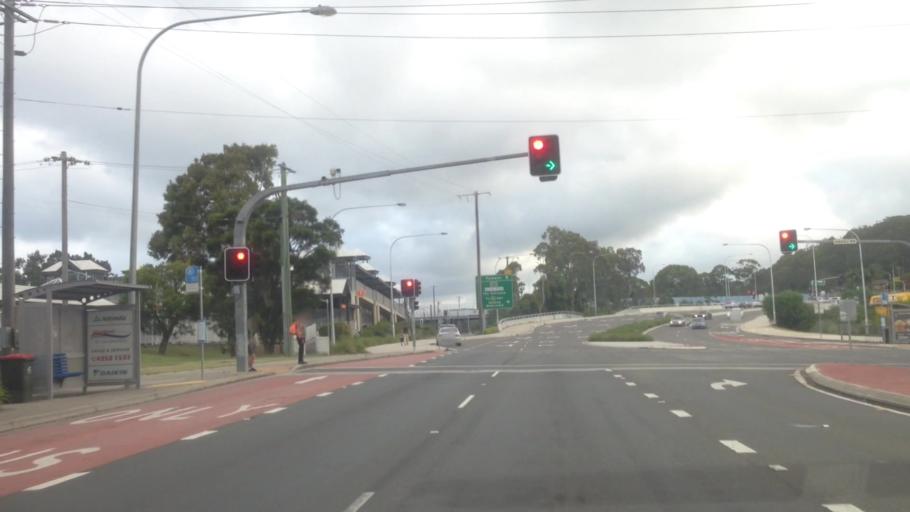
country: AU
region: New South Wales
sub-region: Wyong Shire
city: Chittaway Bay
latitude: -33.3069
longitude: 151.4200
